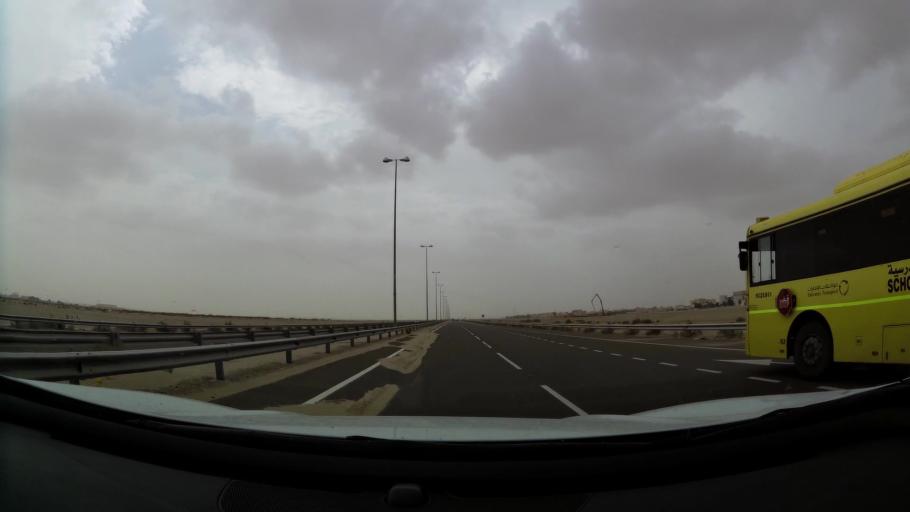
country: AE
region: Abu Dhabi
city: Abu Dhabi
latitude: 24.3677
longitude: 54.6708
